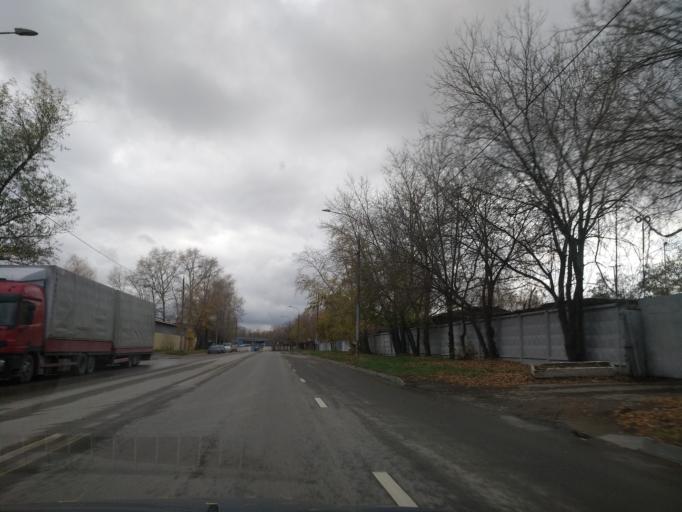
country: RU
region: Moscow
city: Kozeyevo
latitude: 55.8872
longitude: 37.6244
